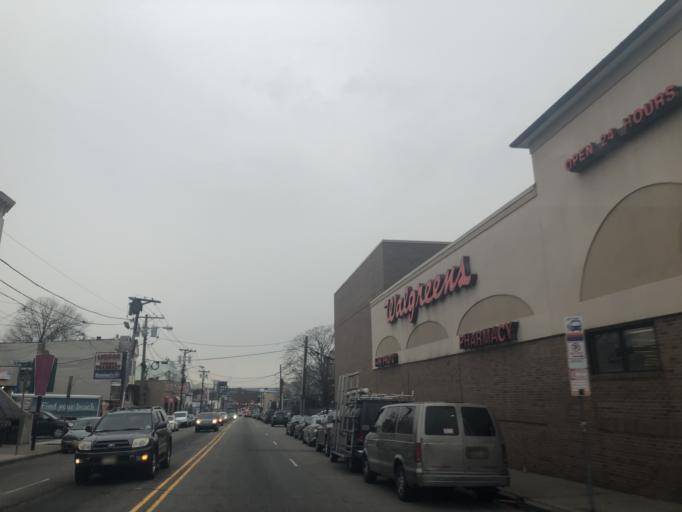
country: US
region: New Jersey
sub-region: Hudson County
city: Jersey City
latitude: 40.7196
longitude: -74.0783
